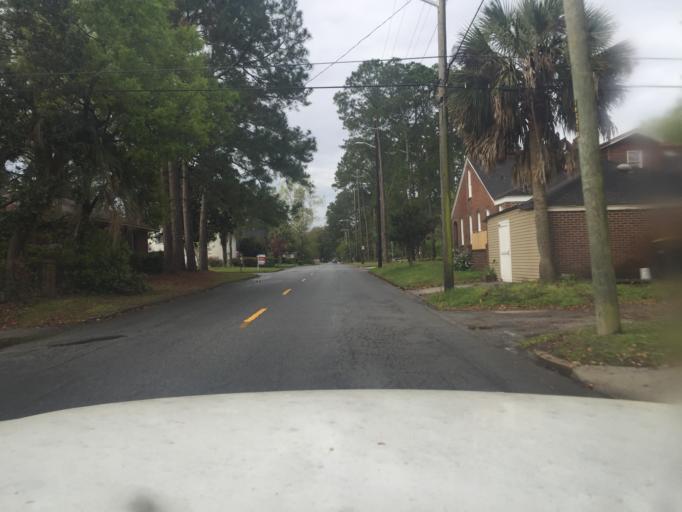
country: US
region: Georgia
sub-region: Chatham County
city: Savannah
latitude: 32.0414
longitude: -81.0920
